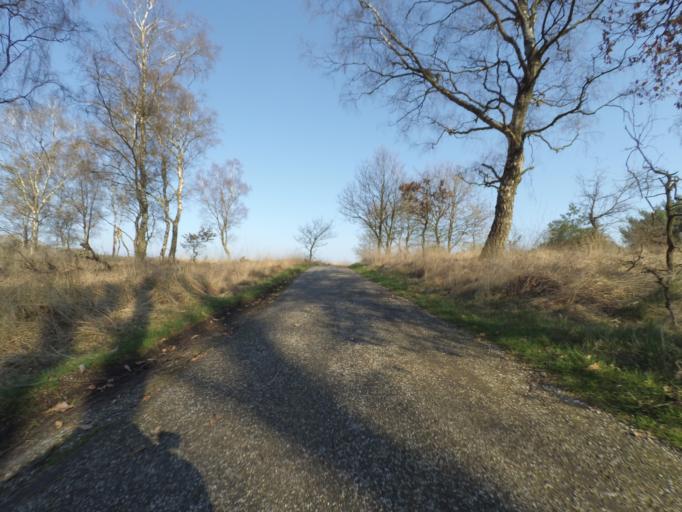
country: NL
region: Gelderland
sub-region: Gemeente Arnhem
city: Hoogkamp
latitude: 52.0613
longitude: 5.8506
